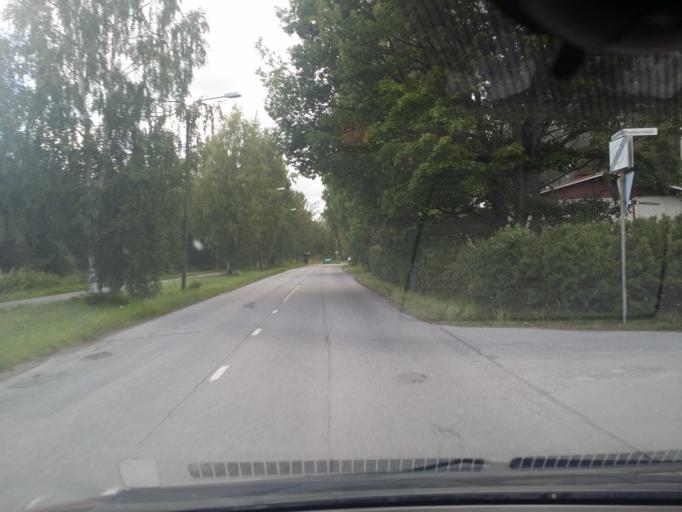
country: FI
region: Satakunta
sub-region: Pori
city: Pori
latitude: 61.5020
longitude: 21.8034
